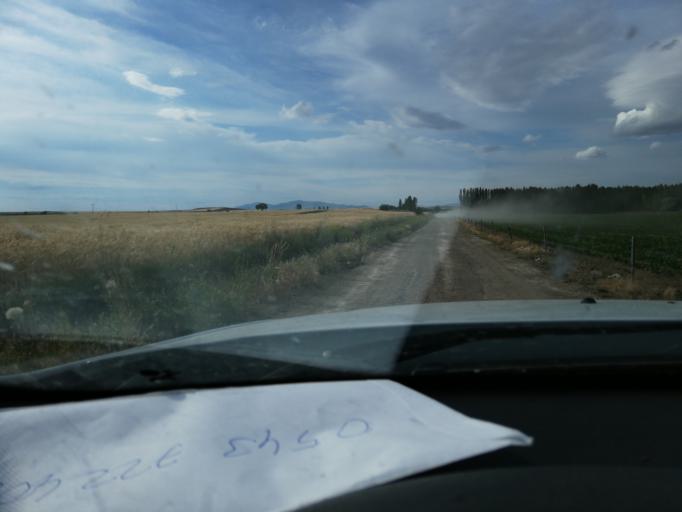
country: TR
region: Kirsehir
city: Kirsehir
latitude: 38.9996
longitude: 34.1245
